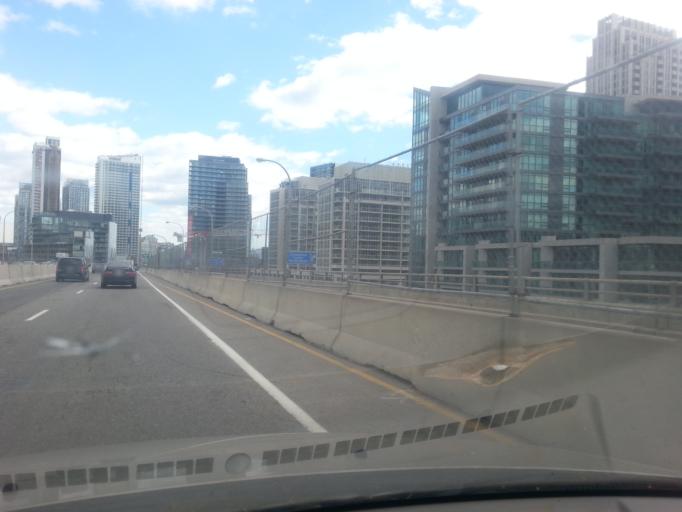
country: CA
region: Ontario
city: Toronto
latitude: 43.6335
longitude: -79.4371
